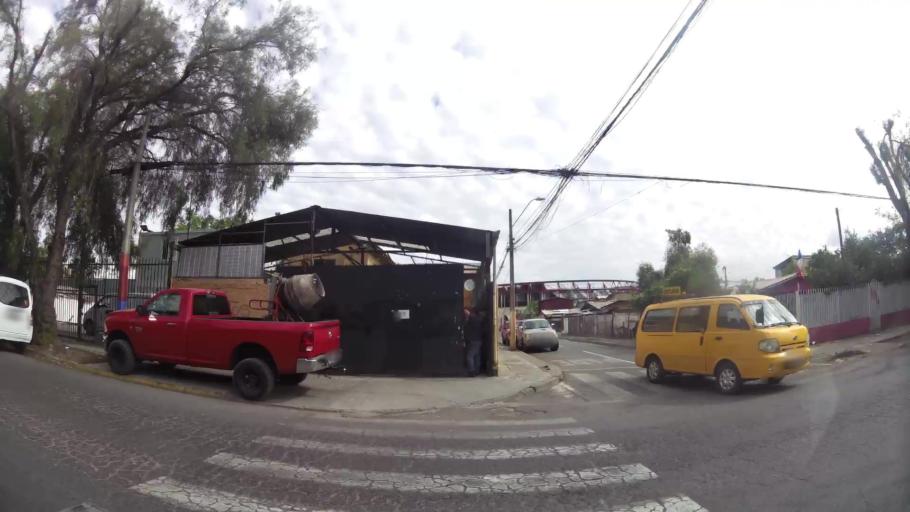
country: CL
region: Santiago Metropolitan
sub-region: Provincia de Santiago
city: La Pintana
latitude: -33.5851
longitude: -70.6371
